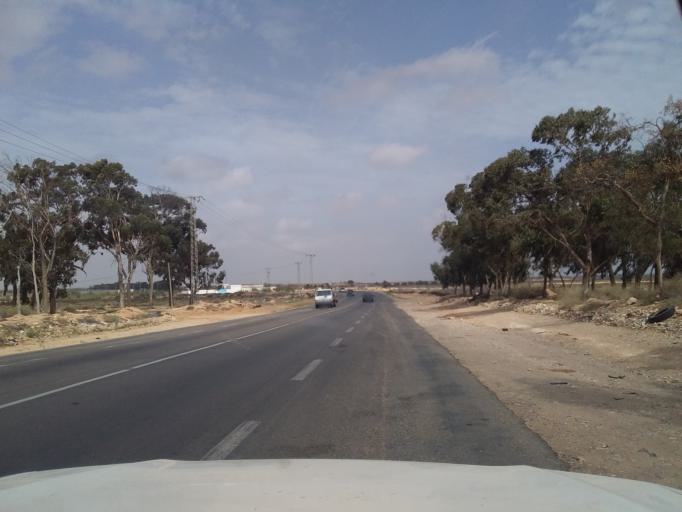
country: TN
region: Qabis
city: Gabes
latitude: 33.6381
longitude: 10.2826
